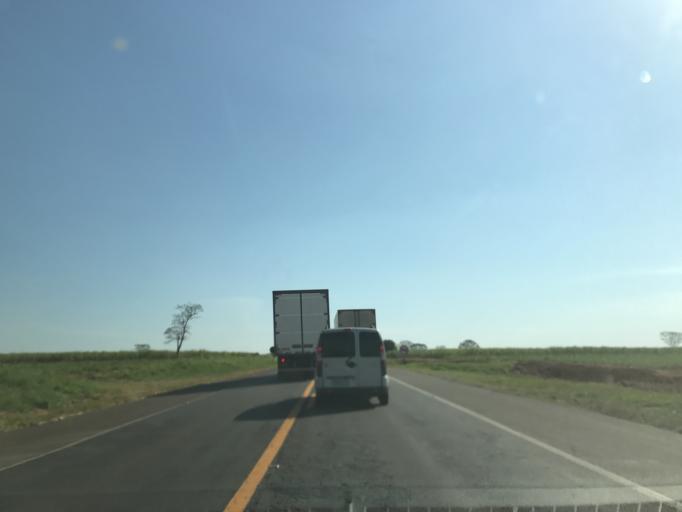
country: BR
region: Sao Paulo
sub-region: Penapolis
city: Penapolis
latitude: -21.4849
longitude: -50.2111
